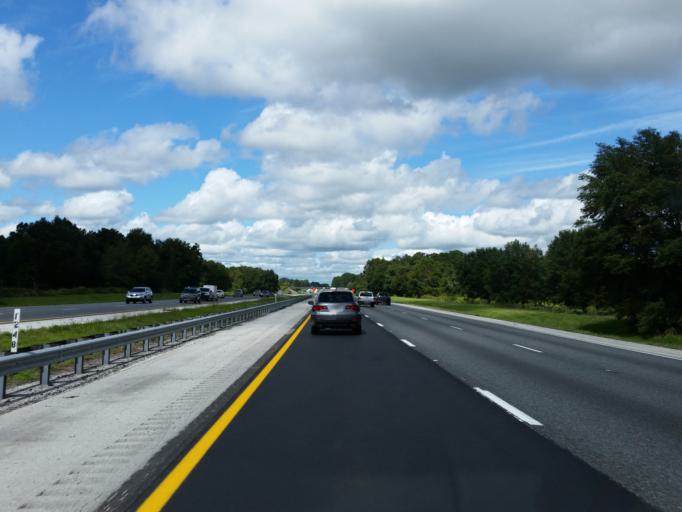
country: US
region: Florida
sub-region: Marion County
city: Ocala
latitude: 29.2884
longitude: -82.2008
